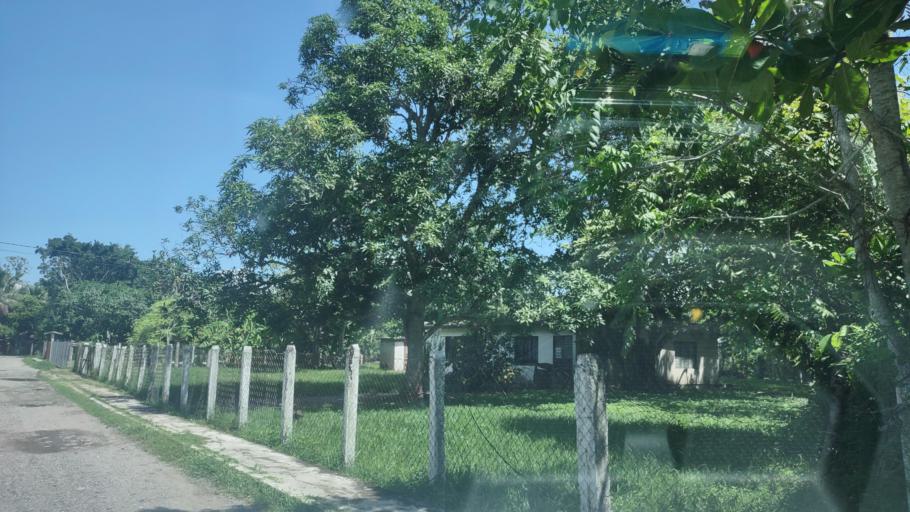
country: MX
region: Veracruz
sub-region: Ozuluama de Mascarenas
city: Cucharas
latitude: 21.5209
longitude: -97.6442
